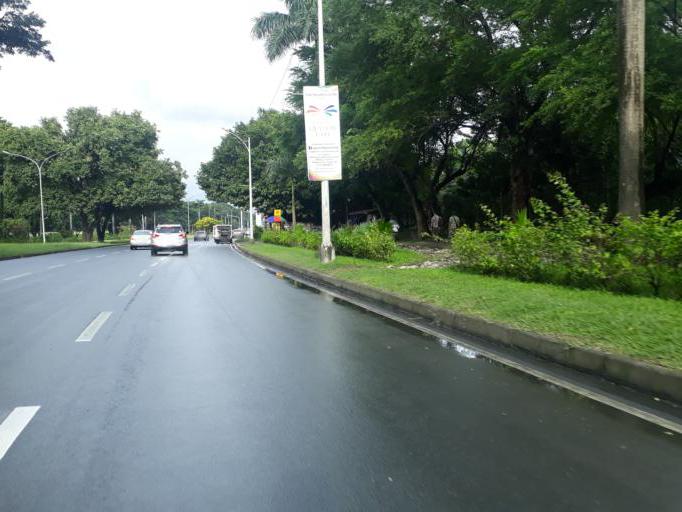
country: PH
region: Metro Manila
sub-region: Quezon City
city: Quezon City
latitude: 14.6545
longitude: 121.0560
